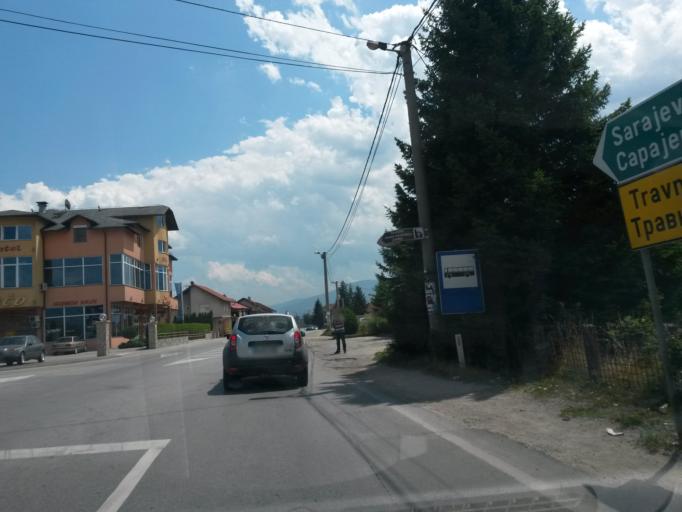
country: BA
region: Federation of Bosnia and Herzegovina
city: Vitez
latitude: 44.1822
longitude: 17.7508
